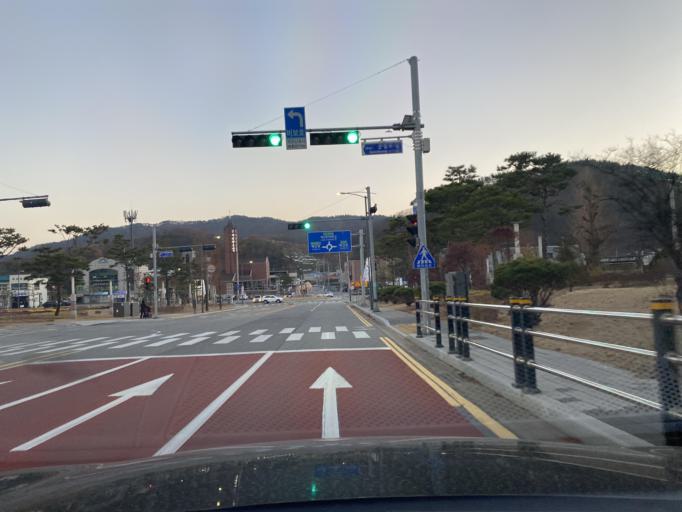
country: KR
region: Chungcheongnam-do
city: Yesan
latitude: 36.6797
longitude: 126.8434
